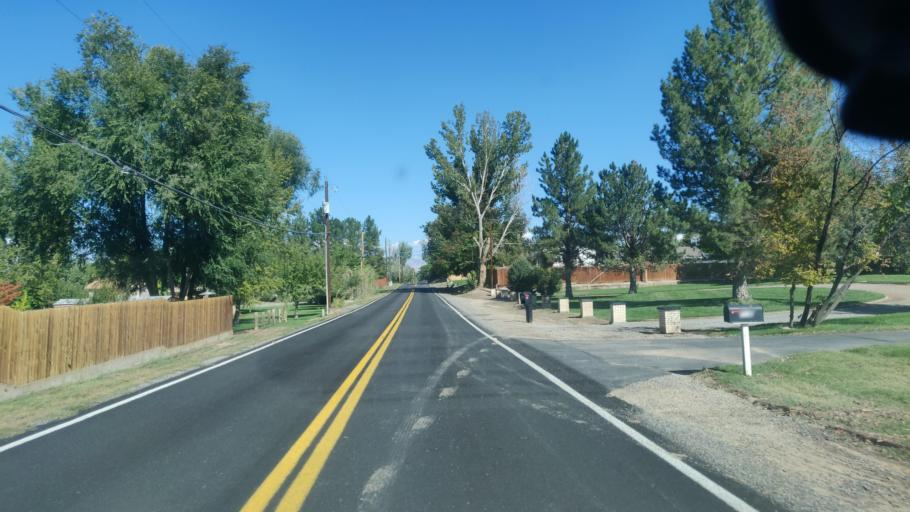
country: US
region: Colorado
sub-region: Mesa County
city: Redlands
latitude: 39.0781
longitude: -108.6265
